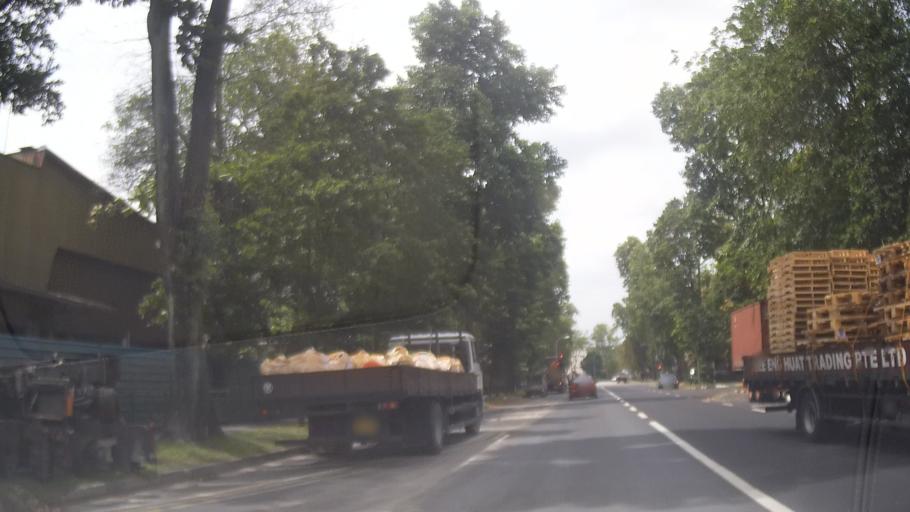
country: MY
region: Johor
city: Johor Bahru
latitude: 1.4162
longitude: 103.7454
